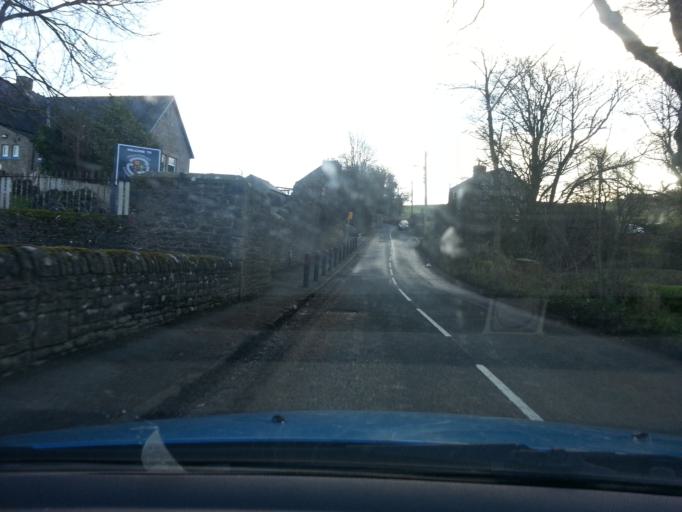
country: GB
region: England
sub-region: County Durham
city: Stanhope
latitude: 54.7243
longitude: -1.9679
